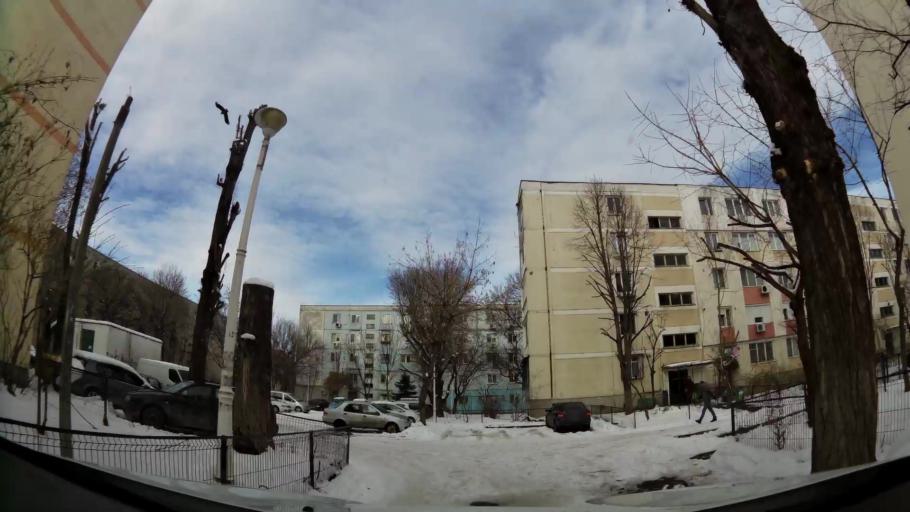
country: RO
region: Bucuresti
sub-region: Municipiul Bucuresti
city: Bucuresti
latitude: 44.3790
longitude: 26.1046
